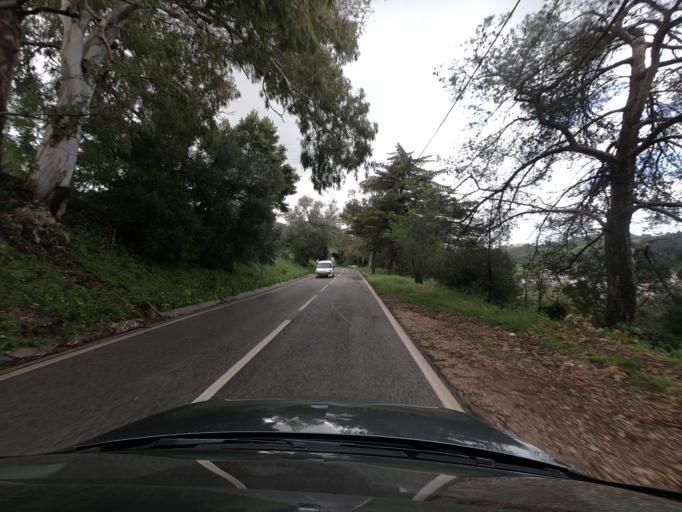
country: PT
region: Lisbon
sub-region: Oeiras
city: Quejas
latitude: 38.7383
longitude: -9.2610
